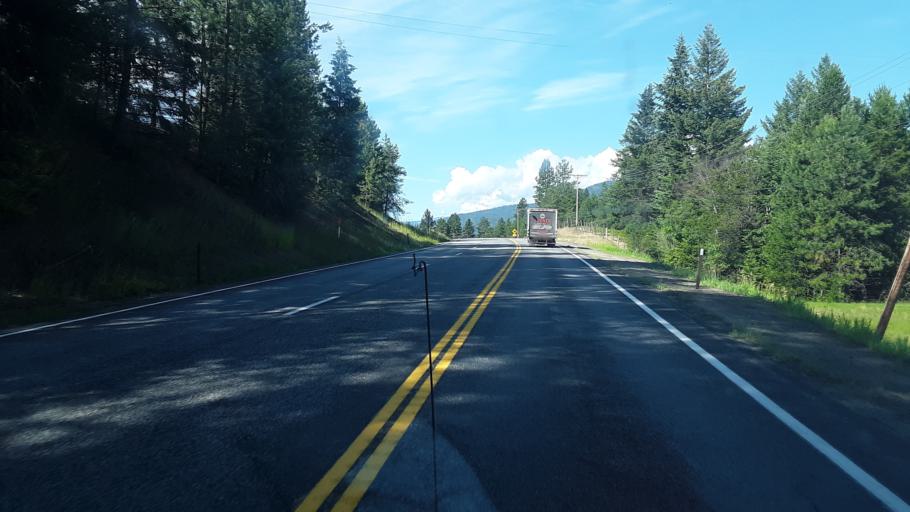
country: US
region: Idaho
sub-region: Boundary County
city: Bonners Ferry
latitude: 48.5258
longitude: -116.4345
